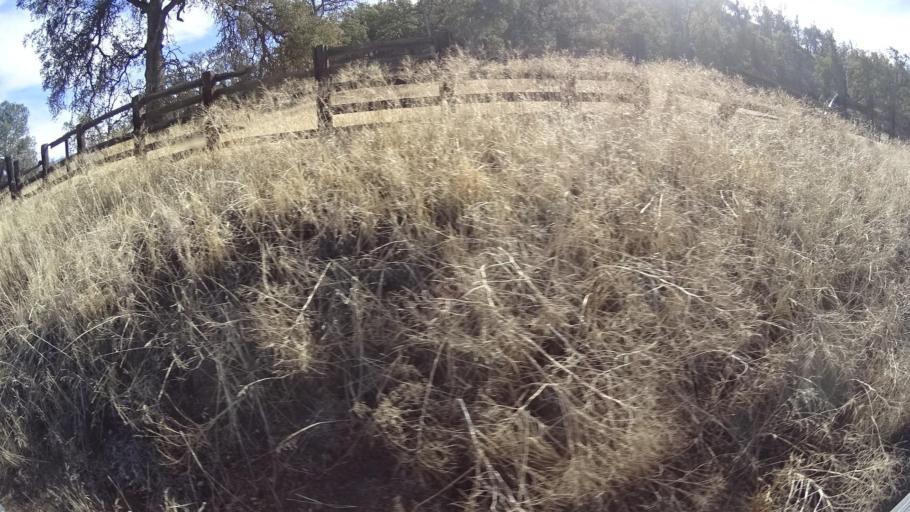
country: US
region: California
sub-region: Kern County
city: Alta Sierra
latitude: 35.7054
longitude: -118.7280
